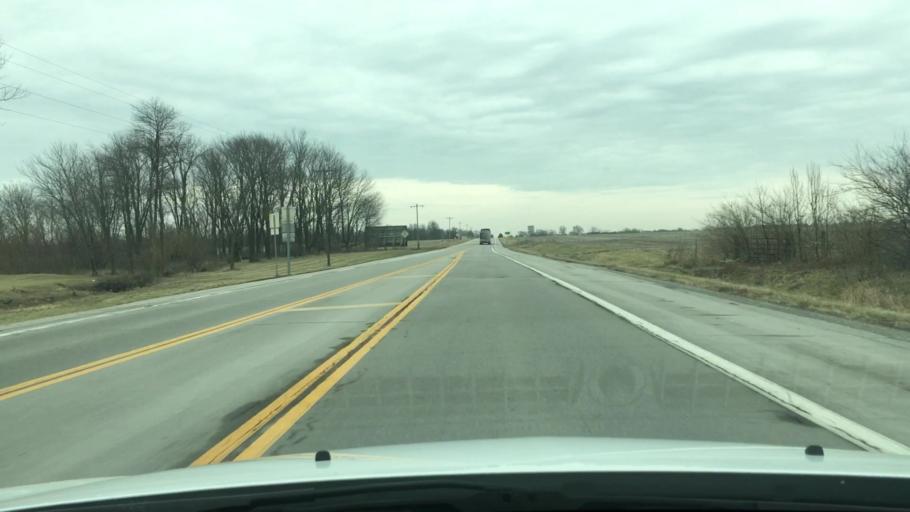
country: US
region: Missouri
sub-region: Audrain County
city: Mexico
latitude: 39.1636
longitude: -91.8195
